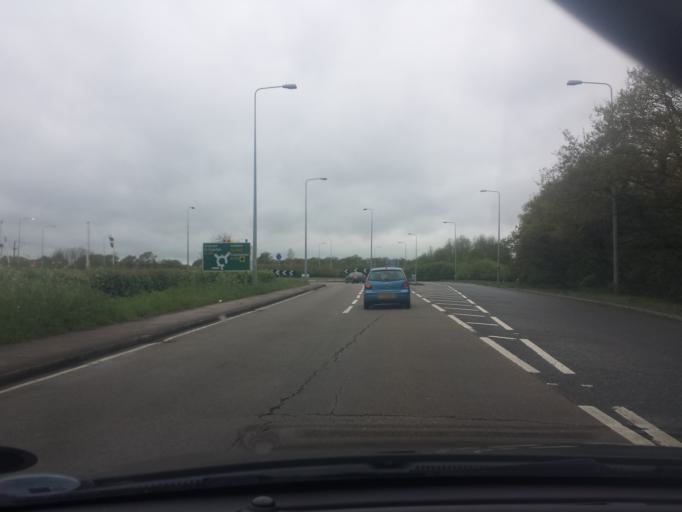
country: GB
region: England
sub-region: Essex
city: Great Bentley
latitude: 51.8599
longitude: 1.1034
